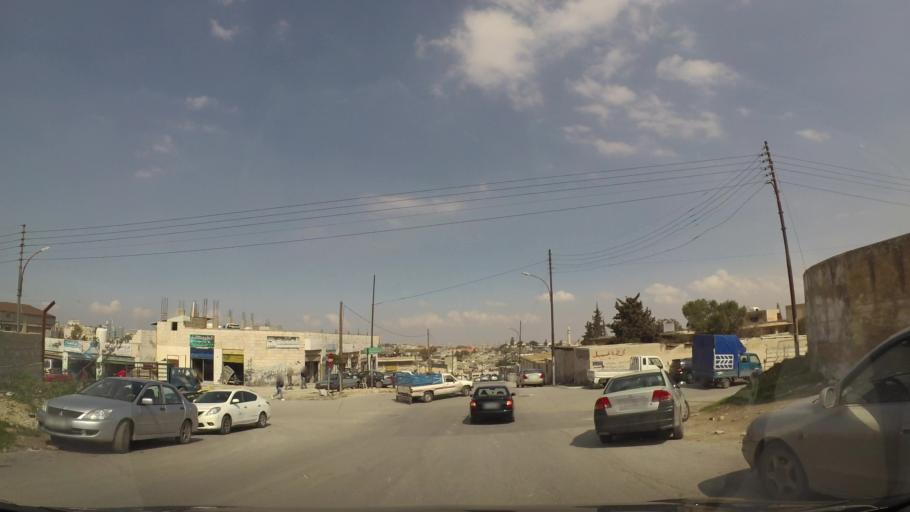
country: JO
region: Zarqa
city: Russeifa
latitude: 31.9898
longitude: 35.9987
